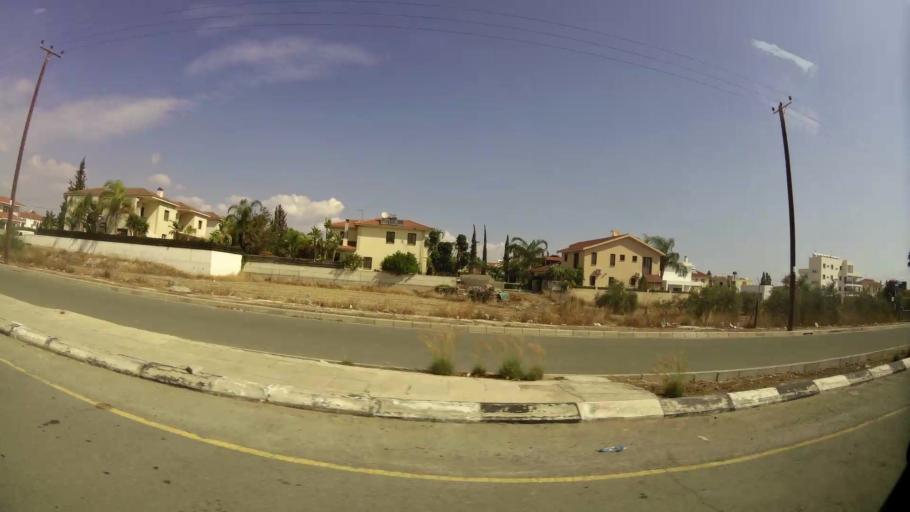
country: CY
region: Larnaka
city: Aradippou
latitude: 34.9393
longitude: 33.5871
